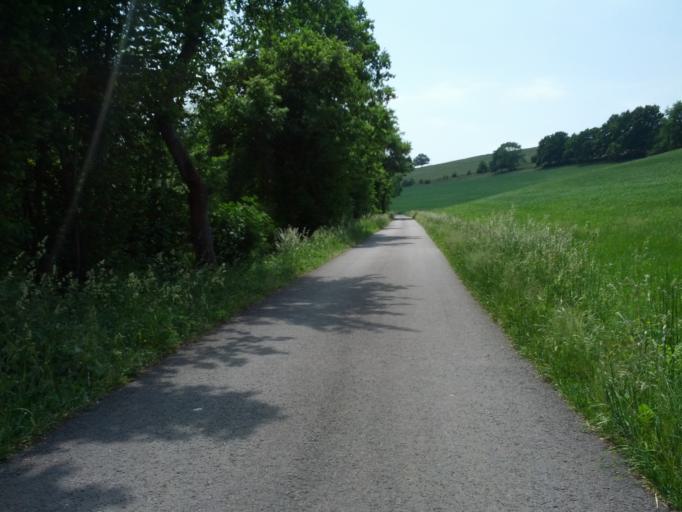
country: DE
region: Thuringia
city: Wiesenthal
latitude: 50.7193
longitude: 10.1637
